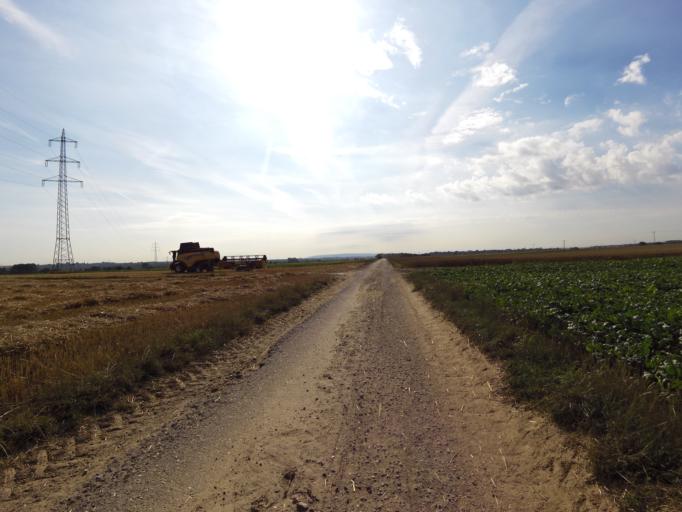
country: DE
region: North Rhine-Westphalia
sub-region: Regierungsbezirk Koln
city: Linnich
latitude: 50.9874
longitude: 6.2475
